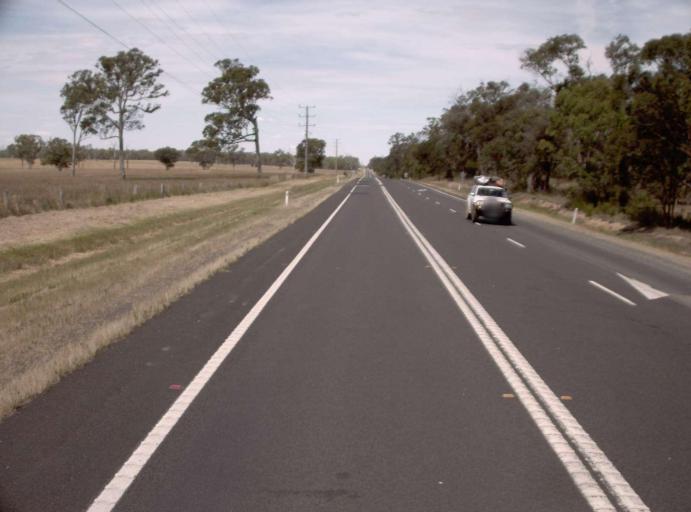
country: AU
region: Victoria
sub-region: Wellington
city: Sale
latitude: -37.9255
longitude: 147.2262
